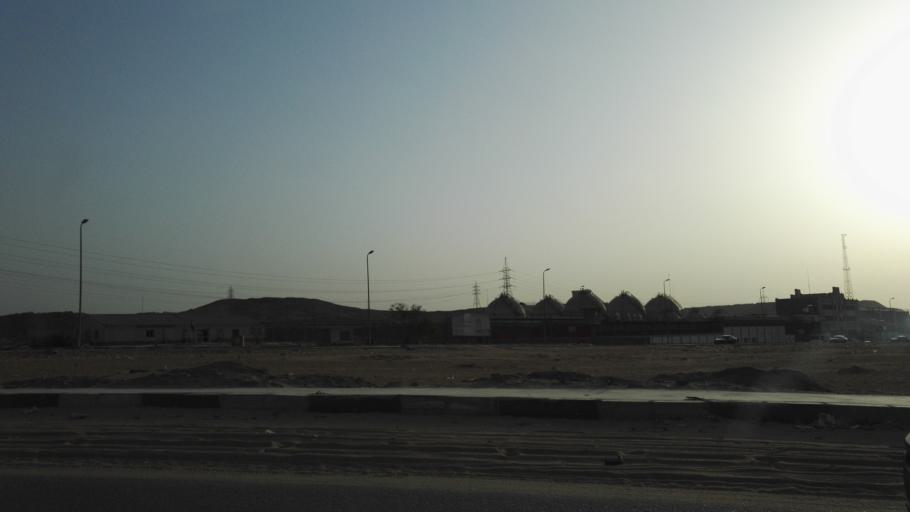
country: EG
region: Al Jizah
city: Al Hawamidiyah
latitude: 29.9784
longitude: 31.3524
